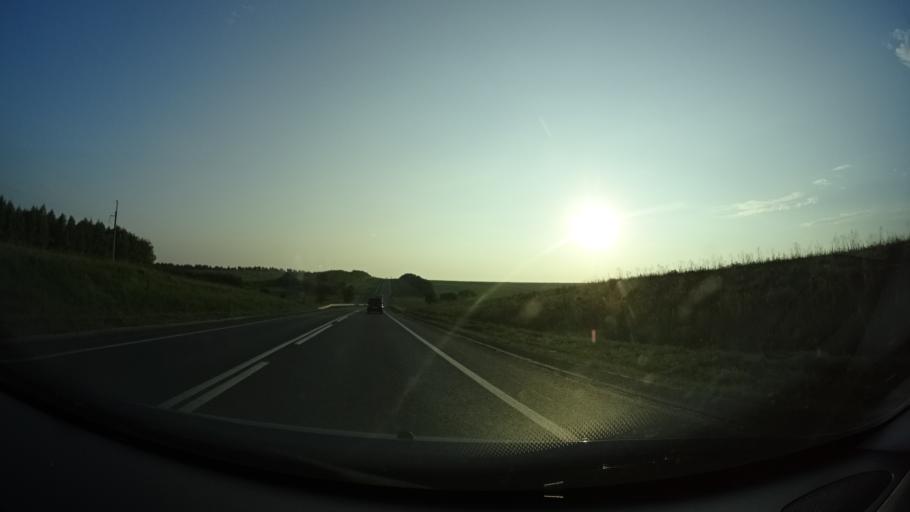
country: RU
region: Samara
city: Kamyshla
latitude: 54.0260
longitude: 51.8832
